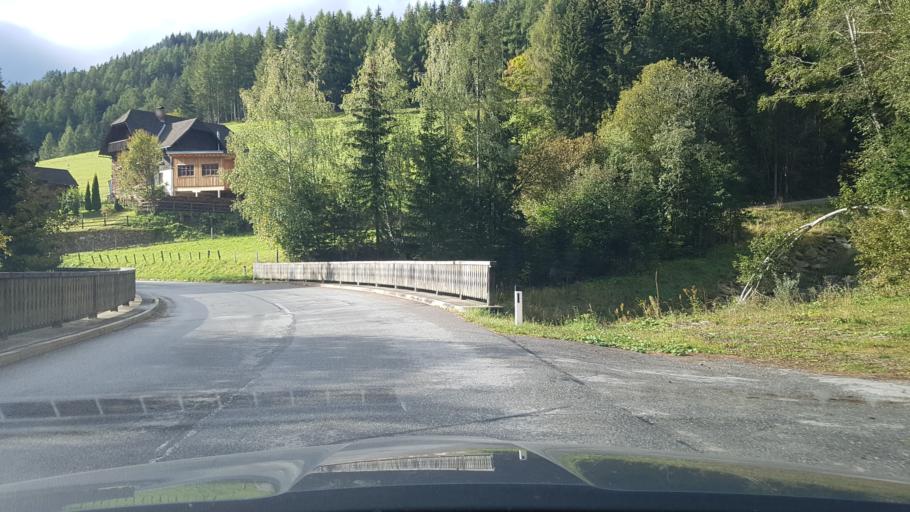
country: AT
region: Styria
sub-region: Politischer Bezirk Murau
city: Schoder
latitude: 47.2063
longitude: 14.1074
